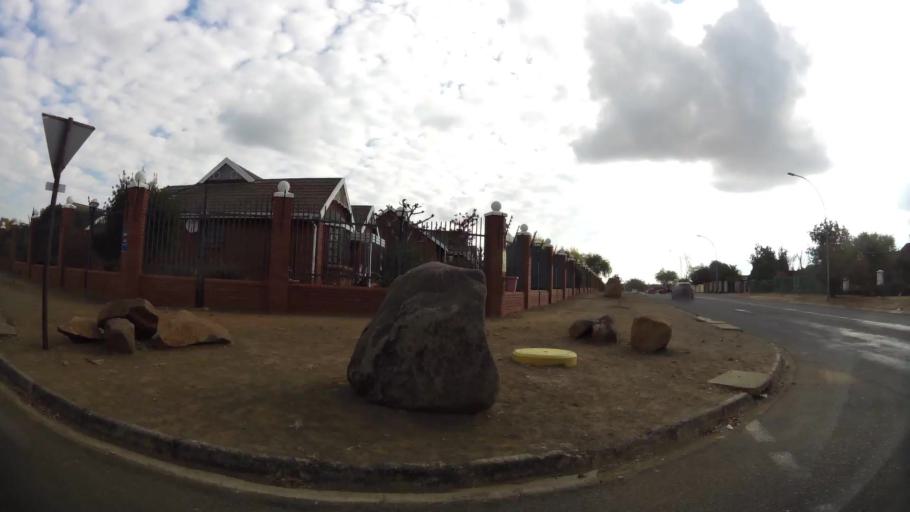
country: ZA
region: Orange Free State
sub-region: Mangaung Metropolitan Municipality
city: Bloemfontein
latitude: -29.0767
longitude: 26.1989
